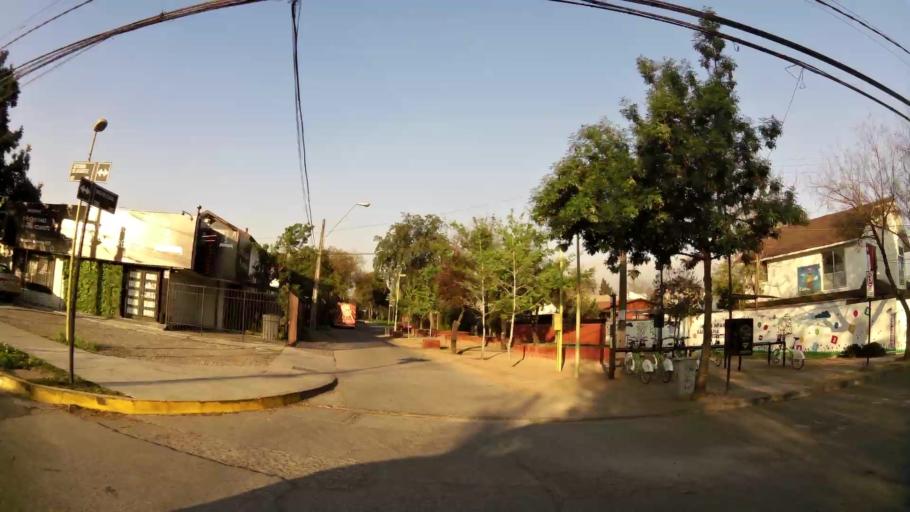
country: CL
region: Santiago Metropolitan
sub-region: Provincia de Santiago
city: Villa Presidente Frei, Nunoa, Santiago, Chile
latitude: -33.3981
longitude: -70.5599
